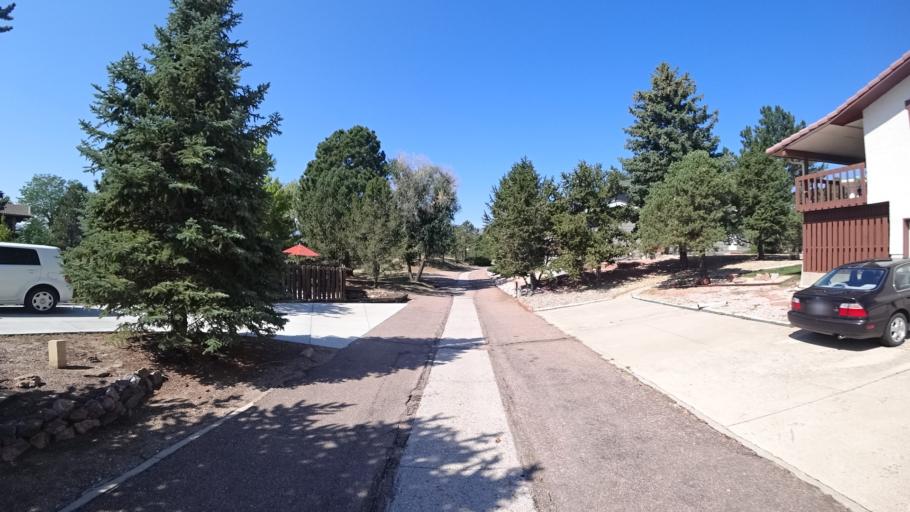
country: US
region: Colorado
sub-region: El Paso County
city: Air Force Academy
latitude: 38.9254
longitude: -104.8208
